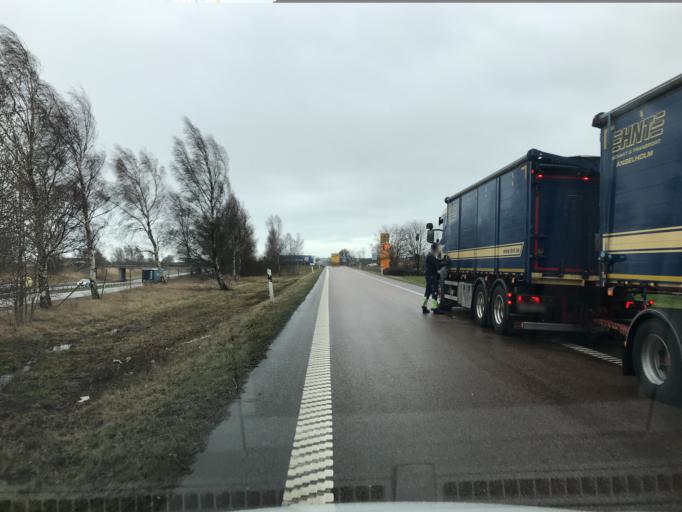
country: SE
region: Skane
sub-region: Angelholms Kommun
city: AEngelholm
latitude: 56.1948
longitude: 12.8581
